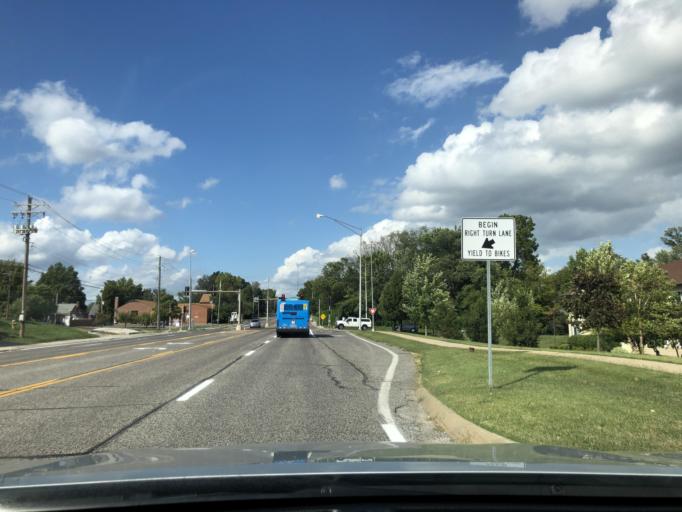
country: US
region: Missouri
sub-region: Saint Louis County
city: Lakeshire
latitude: 38.5431
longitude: -90.3330
